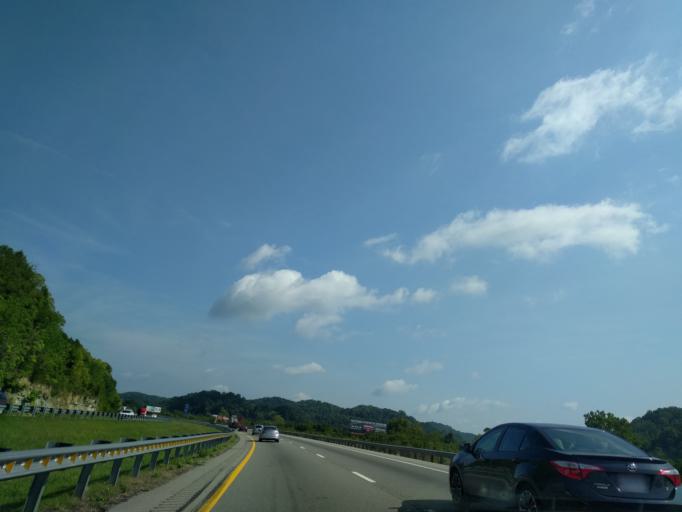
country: US
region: Tennessee
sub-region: Sumner County
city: Millersville
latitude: 36.3706
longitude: -86.7117
